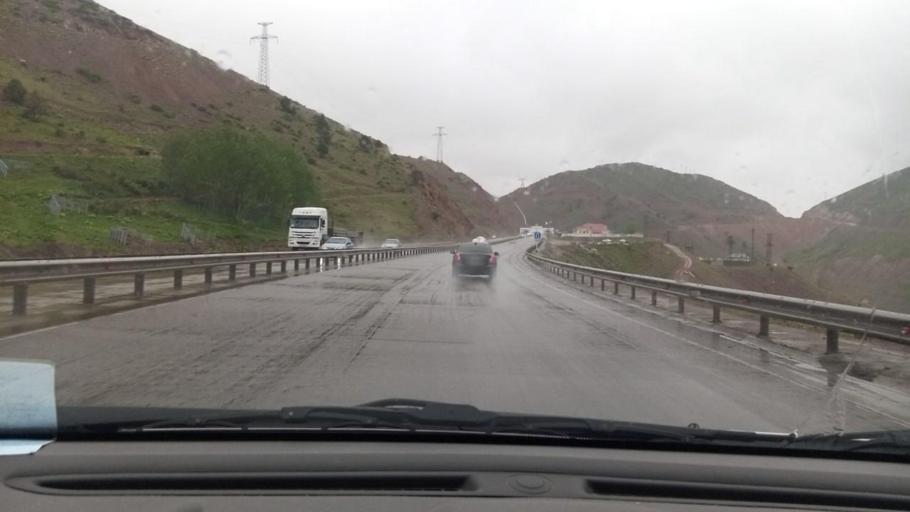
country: UZ
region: Toshkent
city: Angren
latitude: 41.0853
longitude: 70.5381
